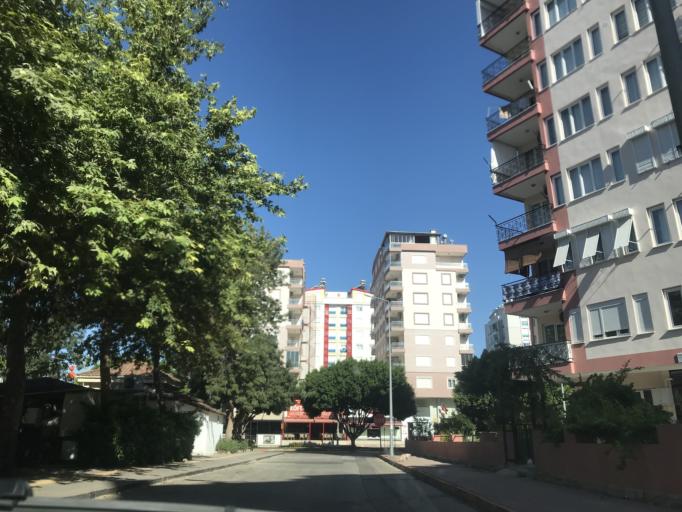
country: TR
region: Antalya
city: Antalya
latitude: 36.8955
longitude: 30.6293
